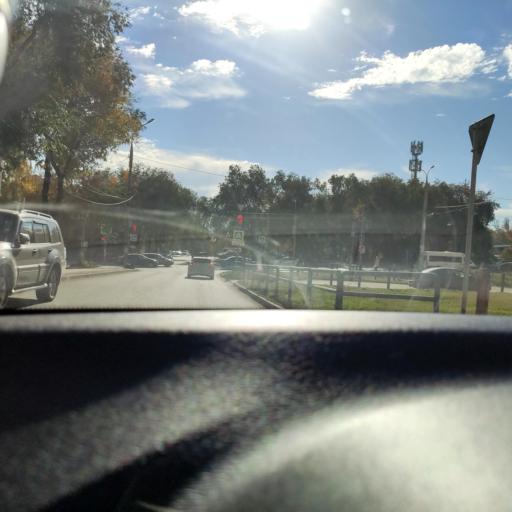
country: RU
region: Samara
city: Samara
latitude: 53.2072
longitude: 50.2210
